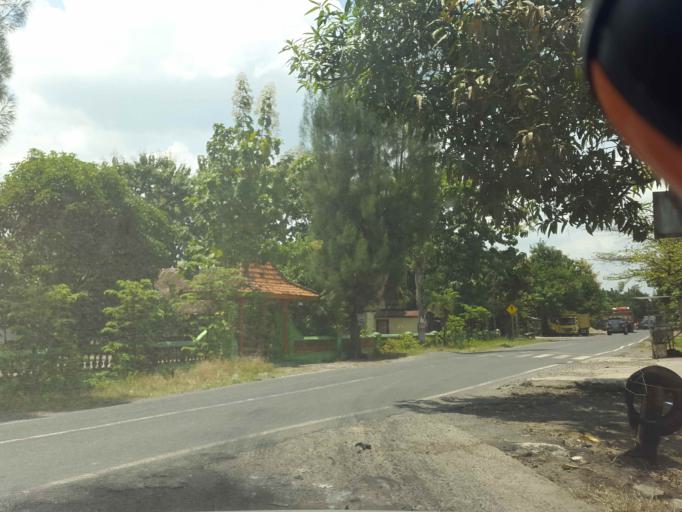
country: ID
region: Central Java
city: Sragen
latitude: -7.3280
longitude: 110.8721
